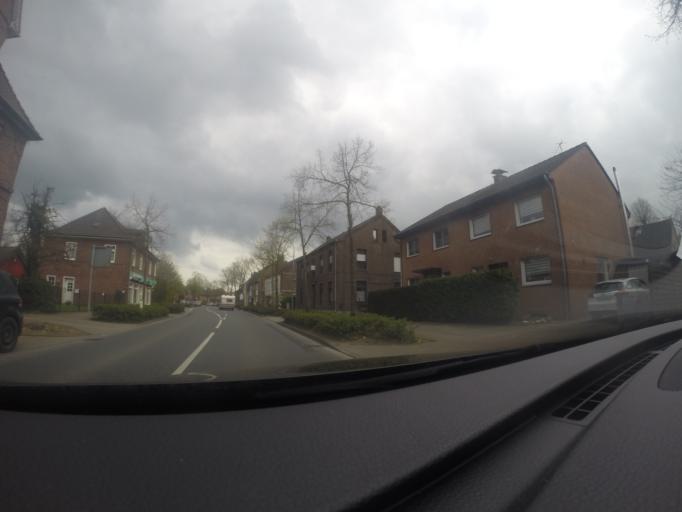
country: DE
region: North Rhine-Westphalia
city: Rees
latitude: 51.6982
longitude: 6.3768
